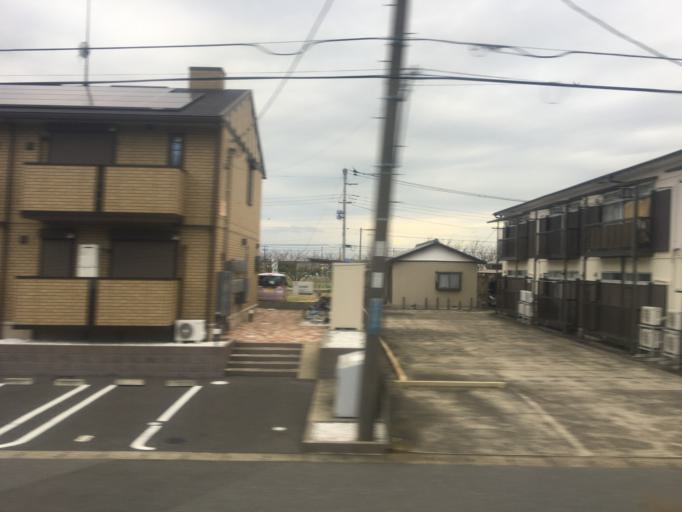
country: JP
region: Chiba
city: Kisarazu
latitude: 35.3641
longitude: 139.9226
